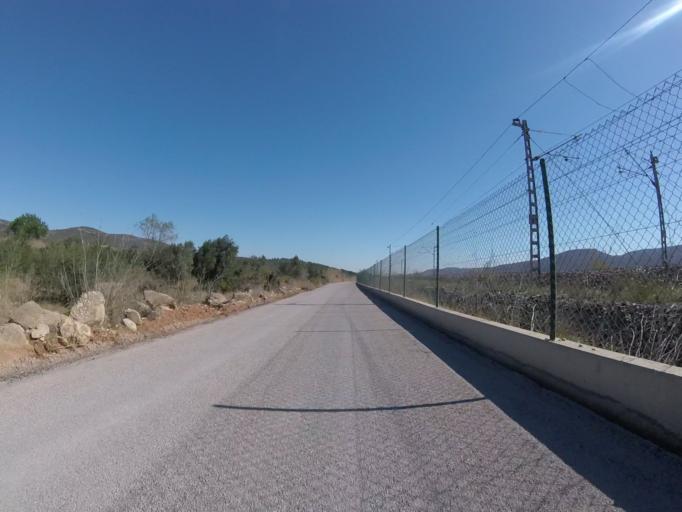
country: ES
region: Valencia
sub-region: Provincia de Castello
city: Alcala de Xivert
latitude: 40.3380
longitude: 0.2577
